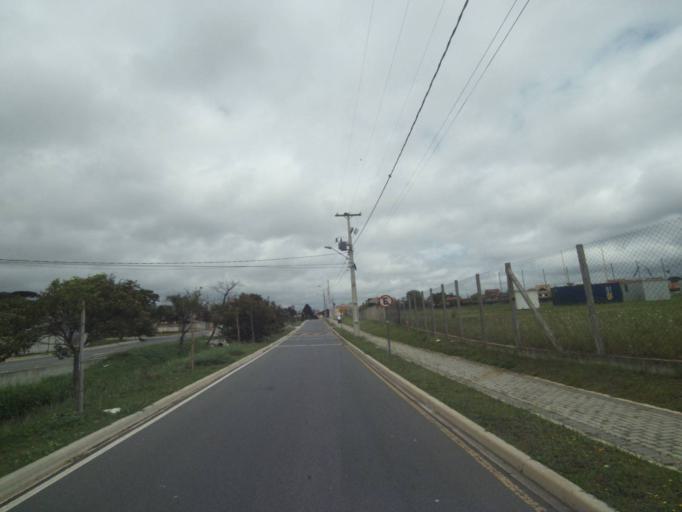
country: BR
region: Parana
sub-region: Pinhais
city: Pinhais
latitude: -25.4331
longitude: -49.2188
